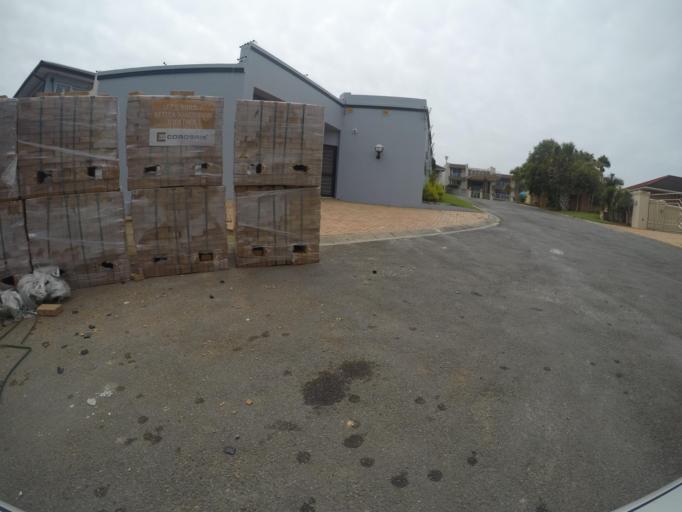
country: ZA
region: Eastern Cape
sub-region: Buffalo City Metropolitan Municipality
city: East London
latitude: -32.9811
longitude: 27.9513
